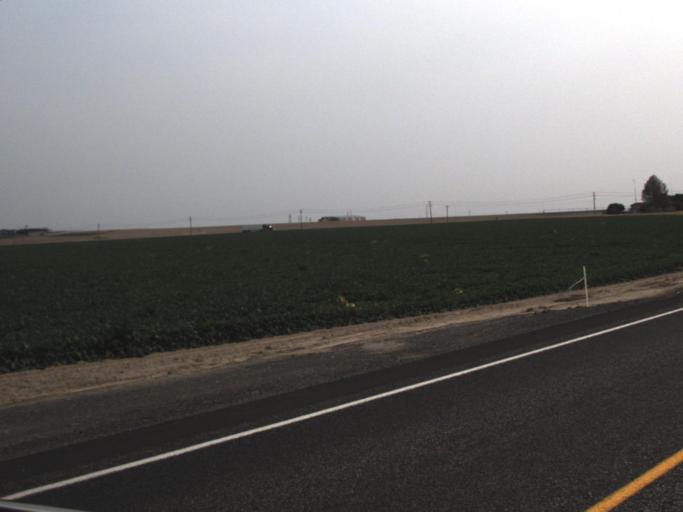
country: US
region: Oregon
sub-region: Morrow County
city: Irrigon
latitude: 46.0620
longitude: -119.6022
